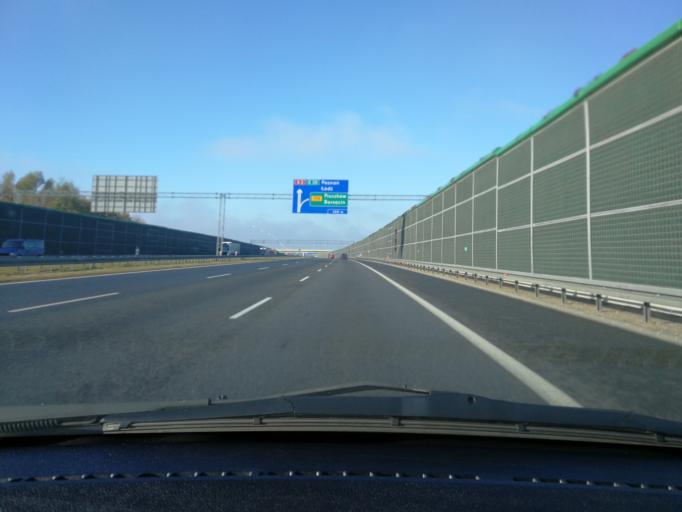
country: PL
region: Masovian Voivodeship
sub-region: Powiat warszawski zachodni
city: Ozarow Mazowiecki
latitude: 52.1929
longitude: 20.8045
